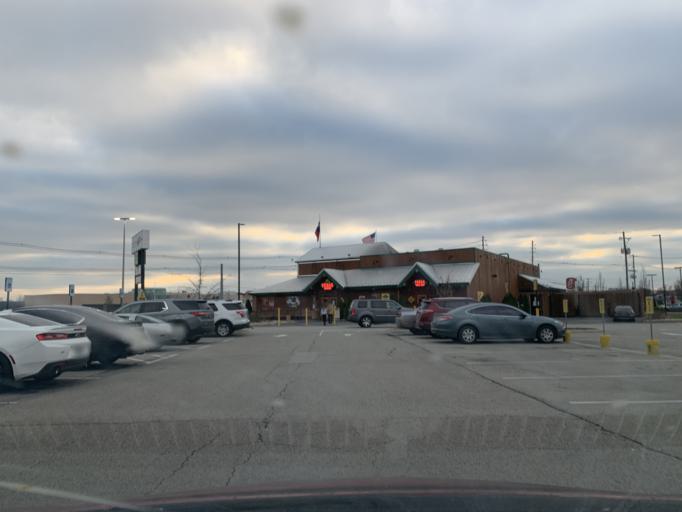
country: US
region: Kentucky
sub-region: Jefferson County
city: Beechwood Village
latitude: 38.2511
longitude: -85.6226
